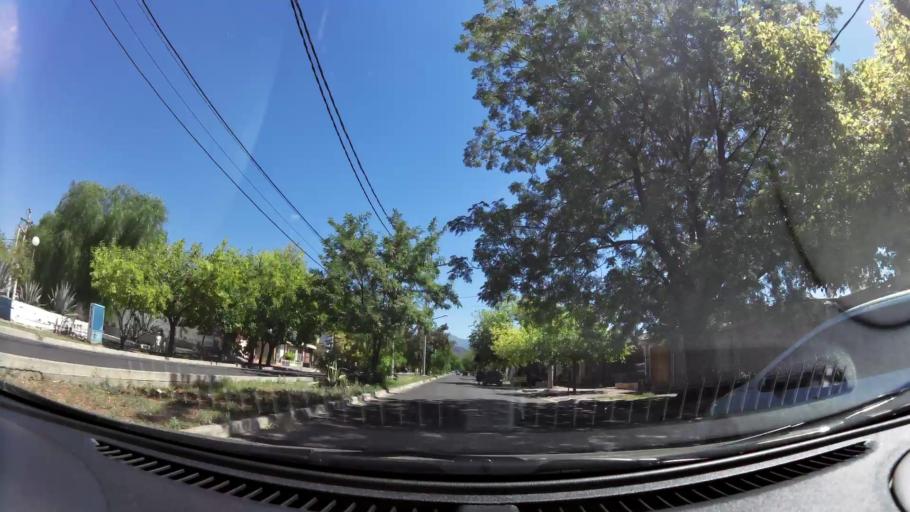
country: AR
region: Mendoza
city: Las Heras
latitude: -32.8583
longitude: -68.8622
